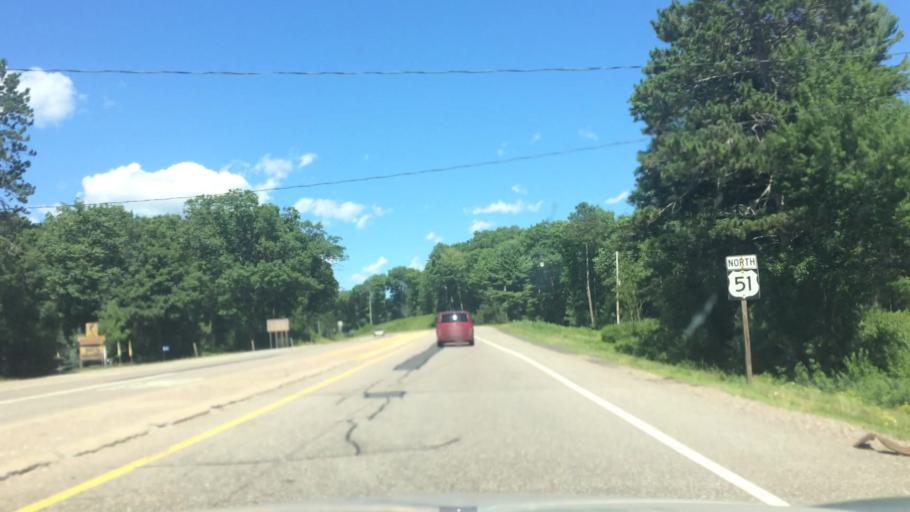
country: US
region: Wisconsin
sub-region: Vilas County
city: Lac du Flambeau
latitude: 45.7858
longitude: -89.7111
